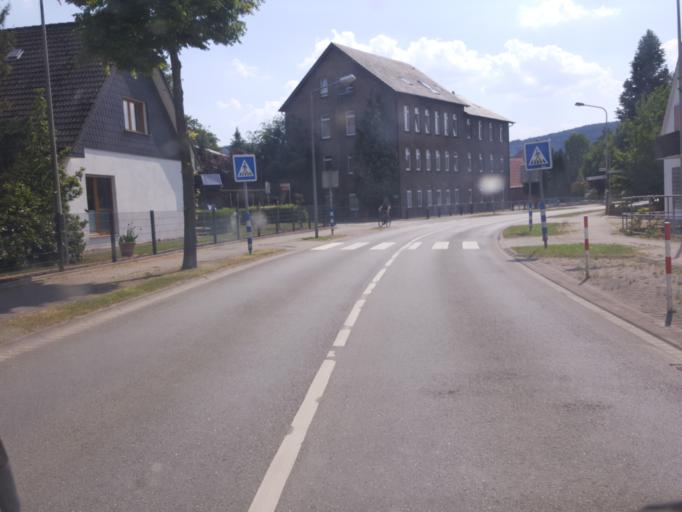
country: DE
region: North Rhine-Westphalia
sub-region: Regierungsbezirk Detmold
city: Hille
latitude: 52.2841
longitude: 8.7912
